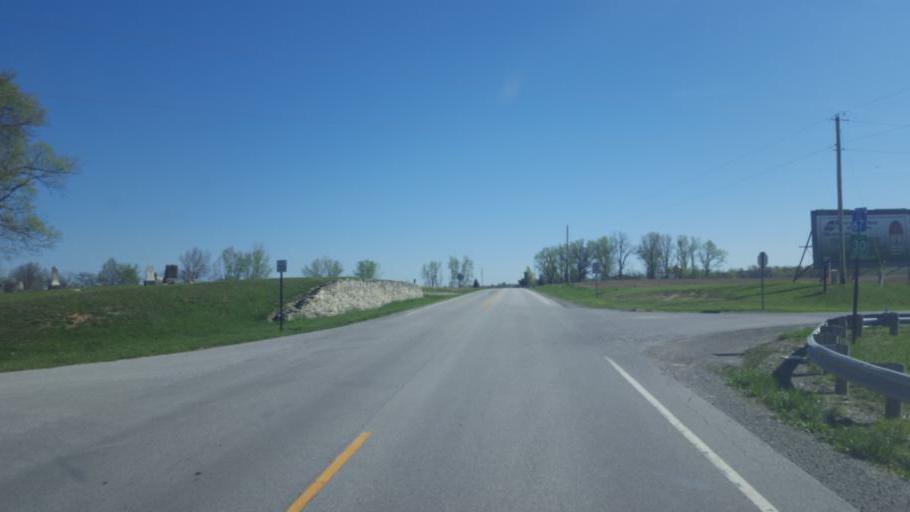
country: US
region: Ohio
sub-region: Wyandot County
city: Upper Sandusky
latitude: 40.9349
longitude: -83.1929
